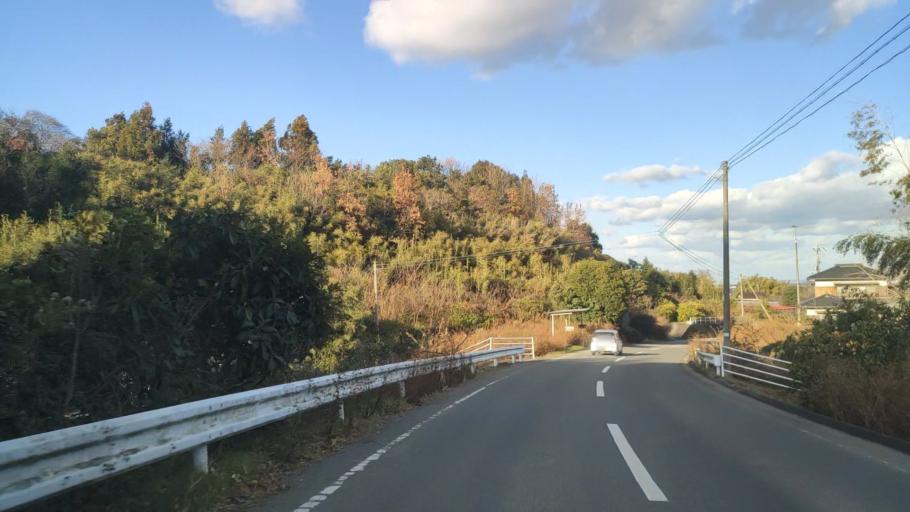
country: JP
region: Ehime
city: Saijo
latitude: 33.8877
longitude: 133.1291
